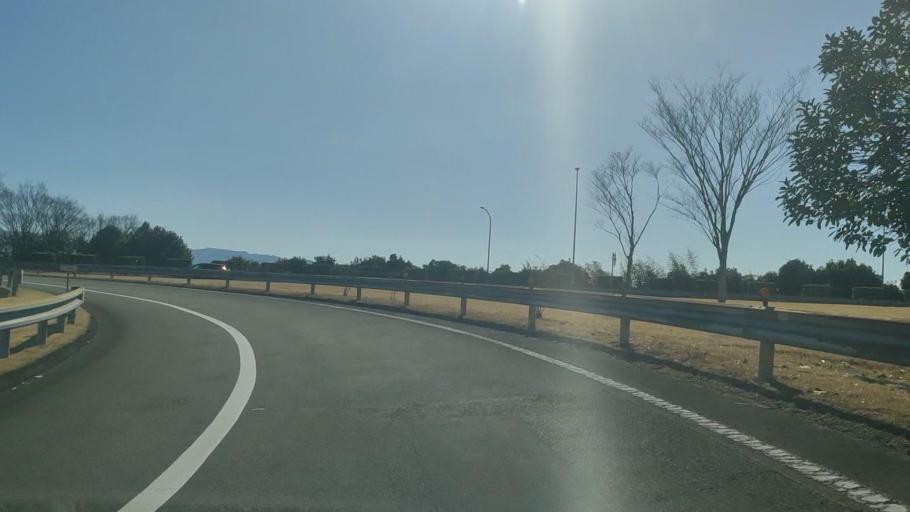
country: JP
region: Miyazaki
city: Miyakonojo
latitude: 31.7829
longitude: 131.1145
